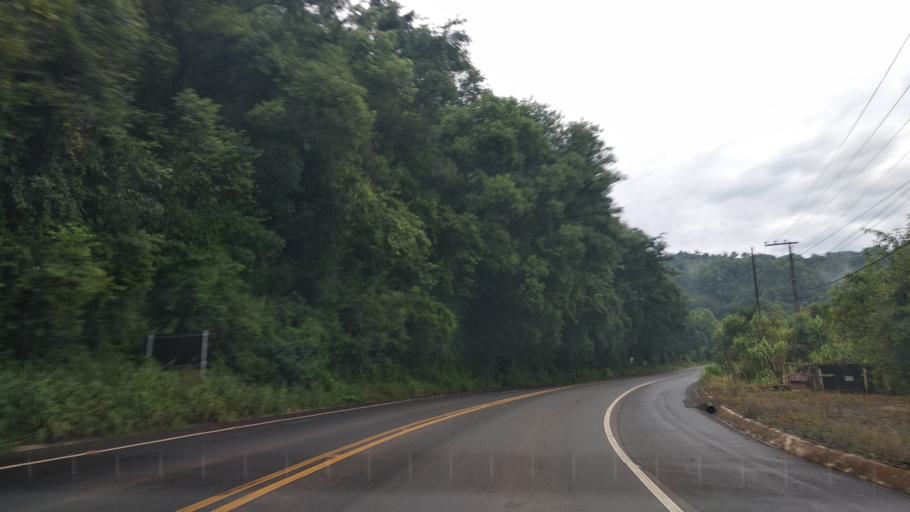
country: BR
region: Santa Catarina
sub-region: Videira
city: Videira
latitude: -27.0592
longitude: -51.2250
